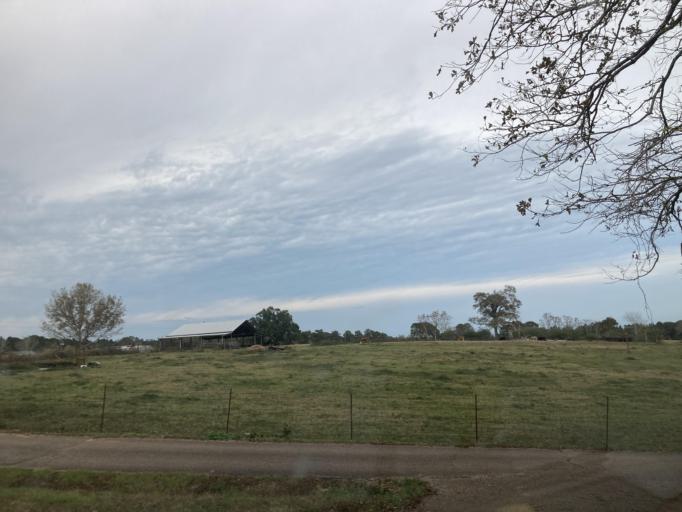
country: US
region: Mississippi
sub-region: Lamar County
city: Purvis
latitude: 31.1674
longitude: -89.3874
